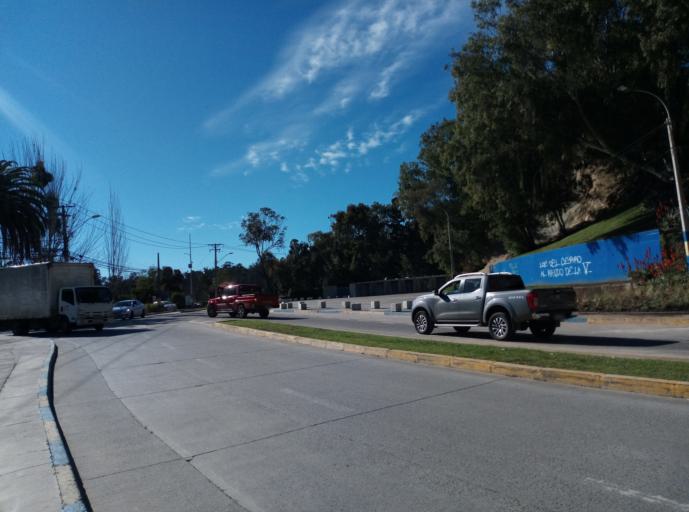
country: CL
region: Valparaiso
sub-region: Provincia de Valparaiso
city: Vina del Mar
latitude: -33.0153
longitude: -71.5377
